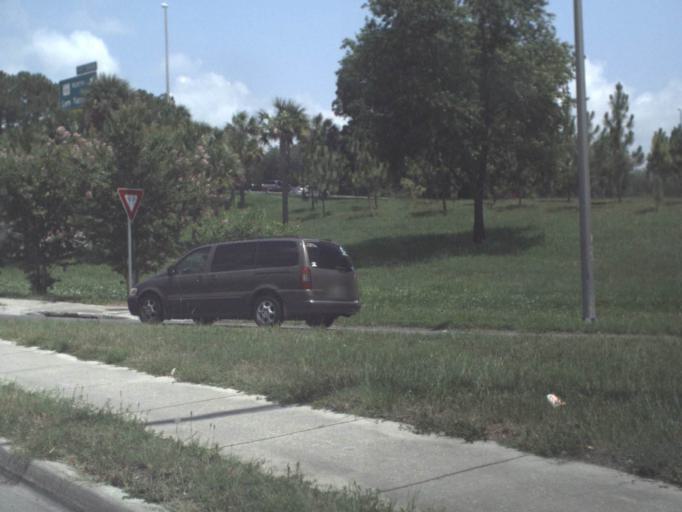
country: US
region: Florida
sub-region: Duval County
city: Jacksonville
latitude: 30.3823
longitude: -81.6722
